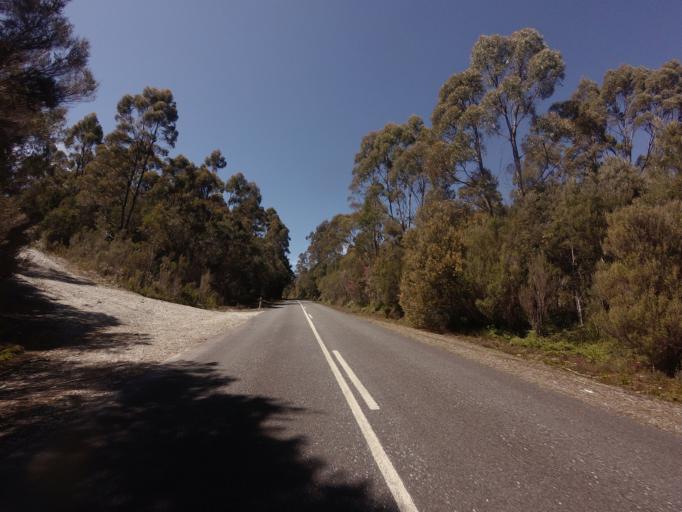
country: AU
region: Tasmania
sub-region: West Coast
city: Queenstown
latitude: -42.7742
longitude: 146.0404
